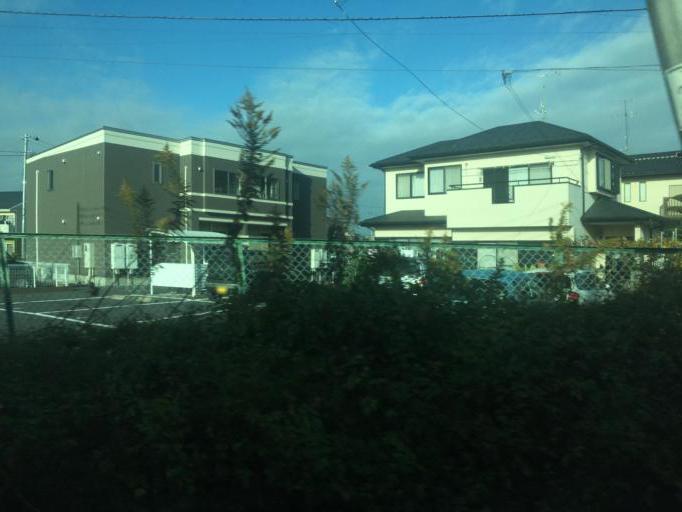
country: JP
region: Ibaraki
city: Ushiku
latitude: 35.9889
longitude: 140.1467
